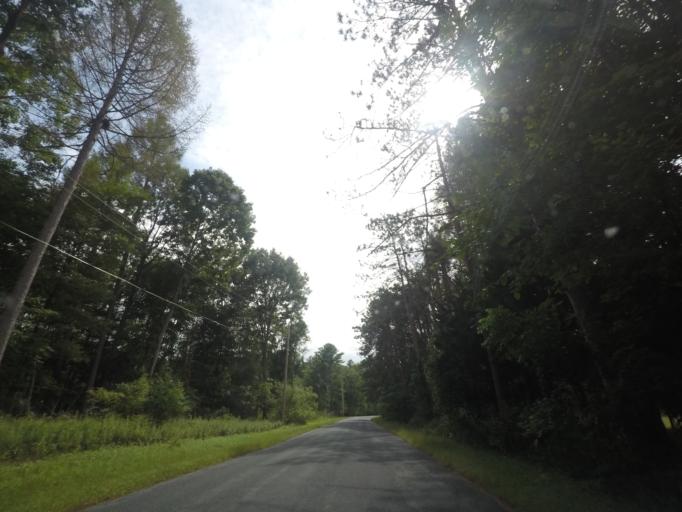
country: US
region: New York
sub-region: Rensselaer County
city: Nassau
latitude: 42.5666
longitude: -73.6158
